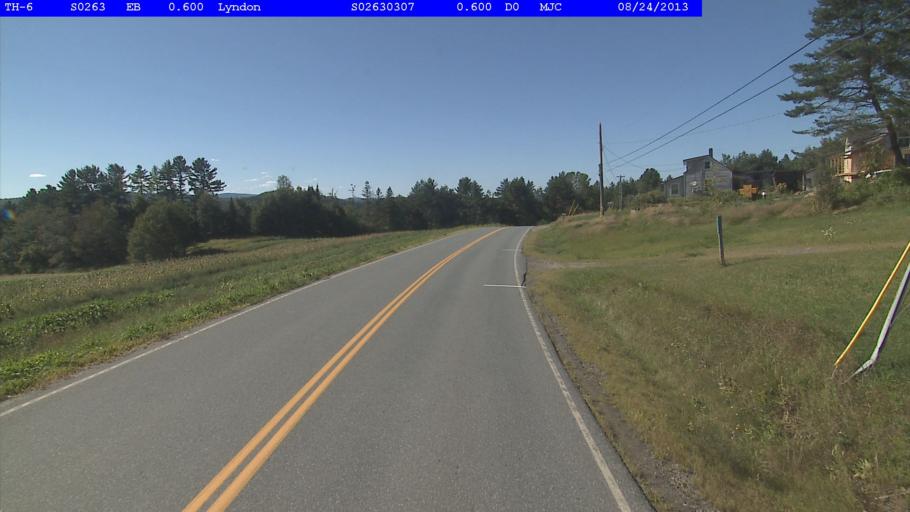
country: US
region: Vermont
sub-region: Caledonia County
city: Lyndon
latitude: 44.4979
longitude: -71.9795
